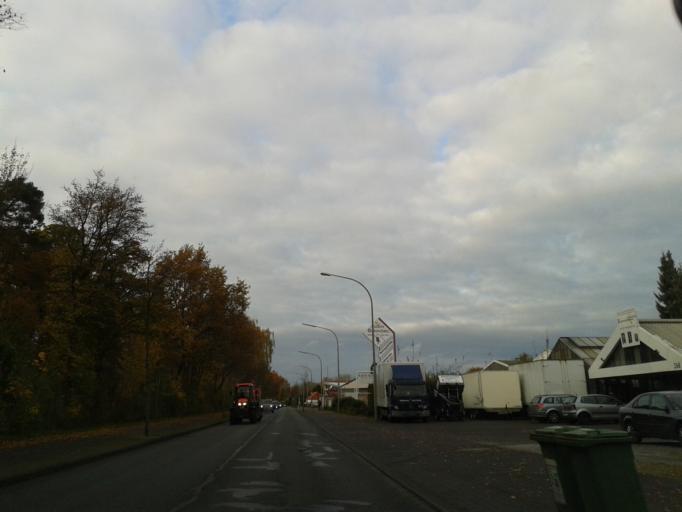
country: DE
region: North Rhine-Westphalia
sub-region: Regierungsbezirk Detmold
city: Paderborn
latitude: 51.7583
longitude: 8.7198
